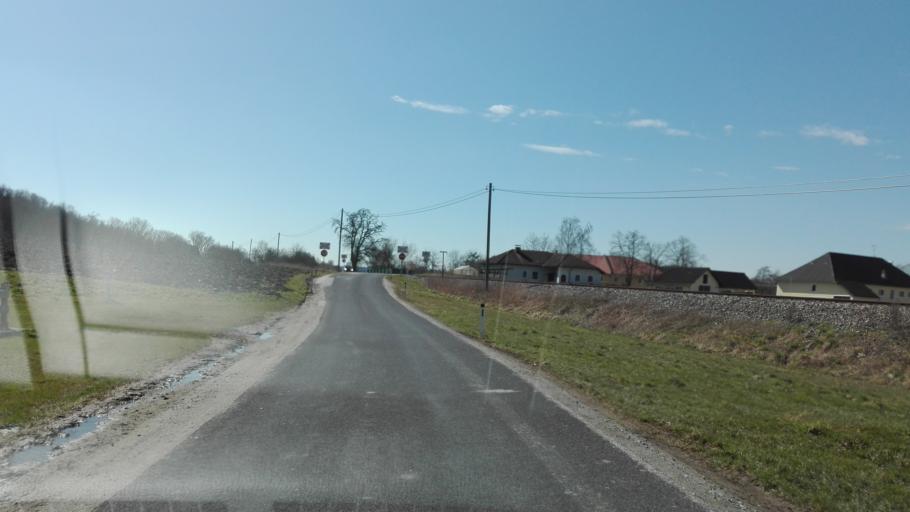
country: AT
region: Upper Austria
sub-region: Wels-Land
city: Buchkirchen
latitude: 48.2421
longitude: 13.9750
